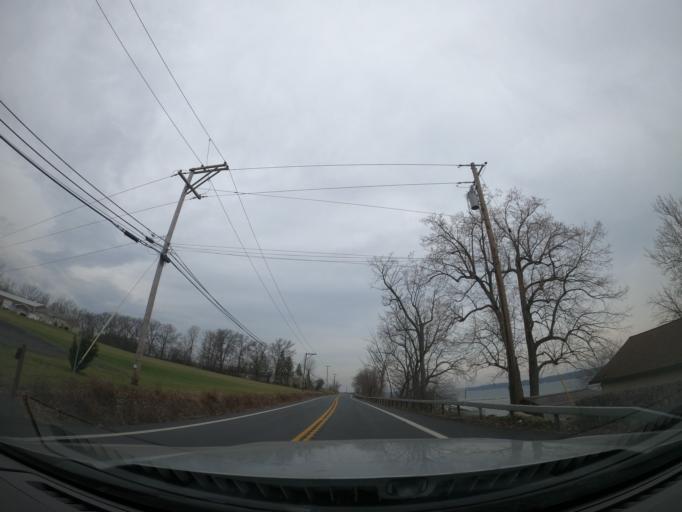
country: US
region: New York
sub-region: Cayuga County
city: Melrose Park
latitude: 42.8597
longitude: -76.5312
